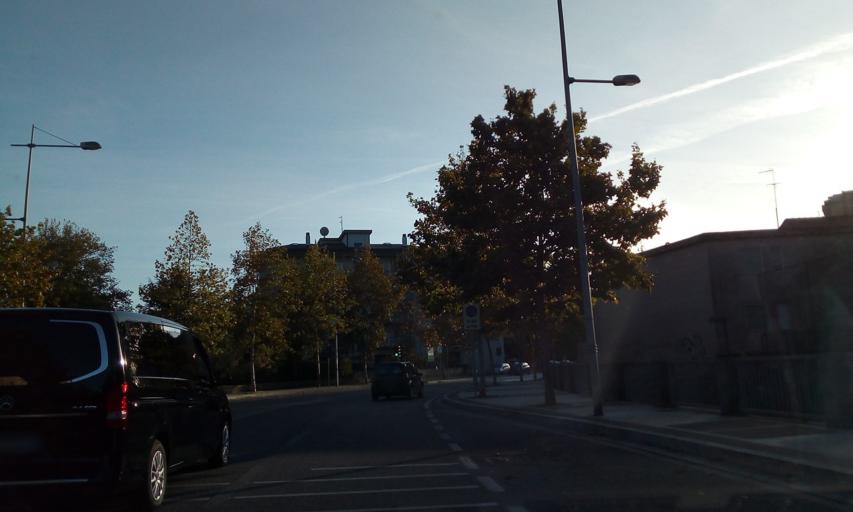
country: IT
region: Campania
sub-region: Provincia di Salerno
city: Capezzano Inferiore
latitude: 40.6916
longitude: 14.7758
